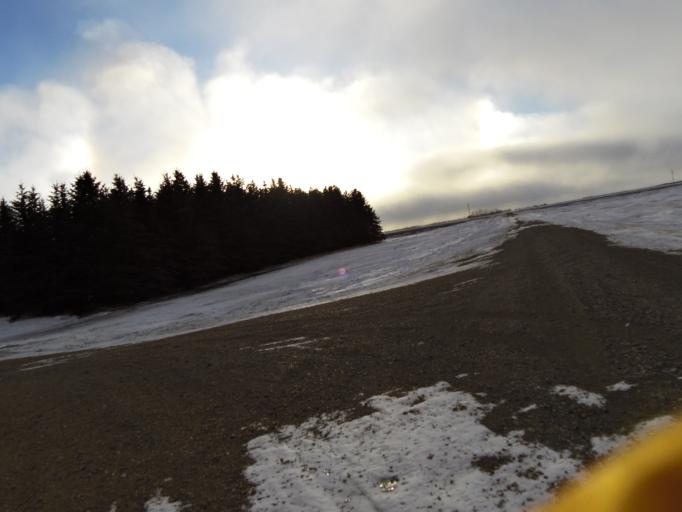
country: US
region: North Dakota
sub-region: Walsh County
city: Grafton
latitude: 48.3976
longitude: -97.2273
